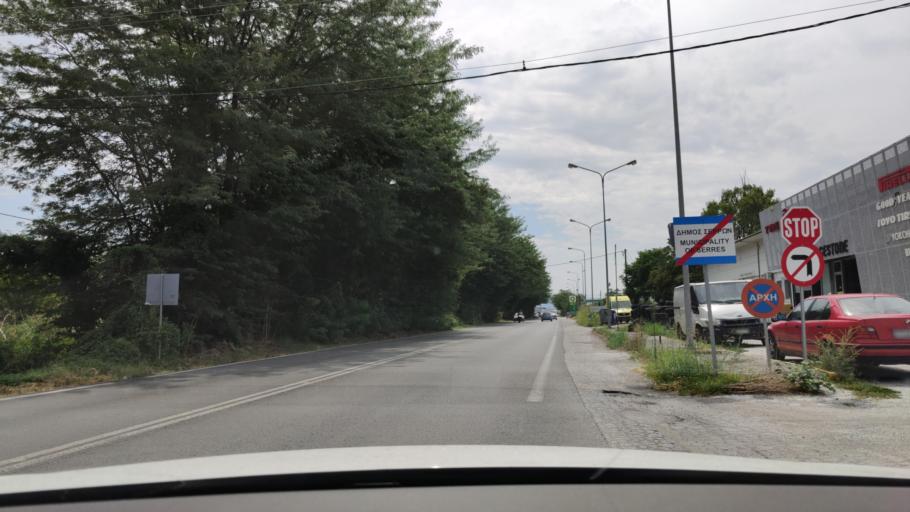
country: GR
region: Central Macedonia
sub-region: Nomos Serron
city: Serres
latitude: 41.0718
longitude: 23.5404
